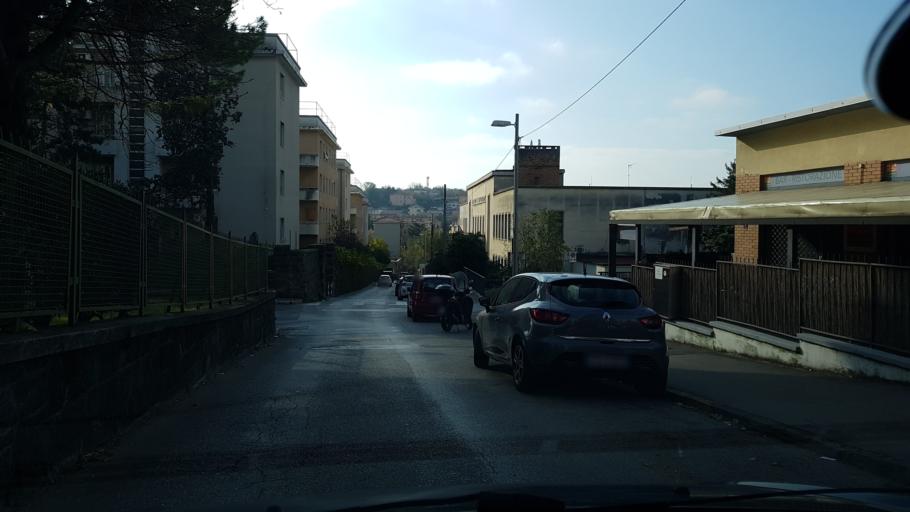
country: IT
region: Friuli Venezia Giulia
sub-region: Provincia di Trieste
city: Trieste
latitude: 45.6236
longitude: 13.7993
